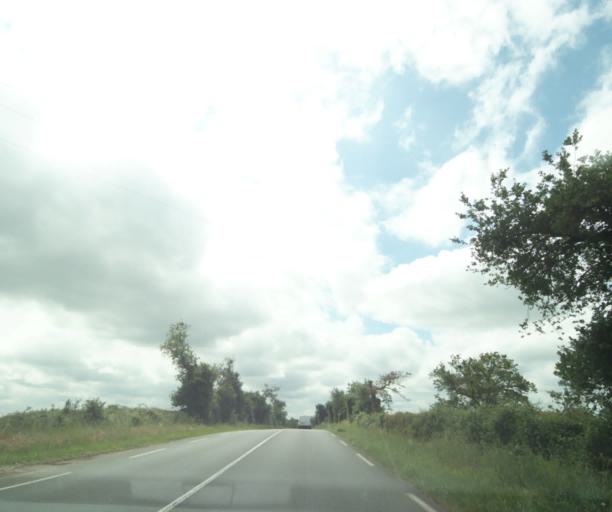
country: FR
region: Poitou-Charentes
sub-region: Departement des Deux-Sevres
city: Viennay
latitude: 46.7155
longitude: -0.2392
